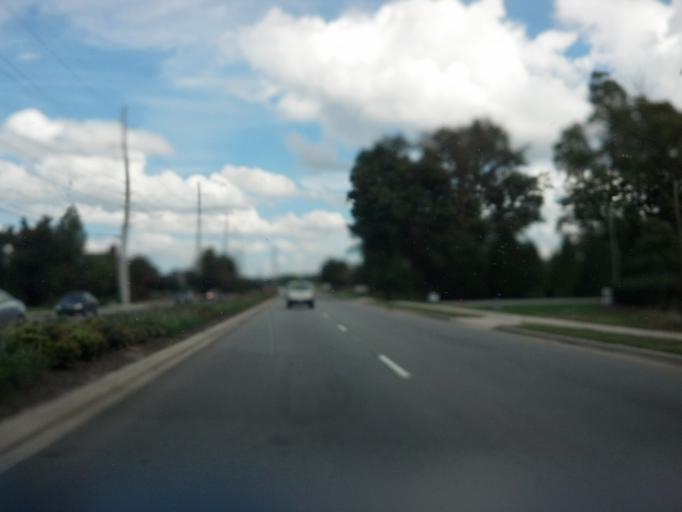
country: US
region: North Carolina
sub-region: Pitt County
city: Windsor
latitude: 35.5536
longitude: -77.3774
